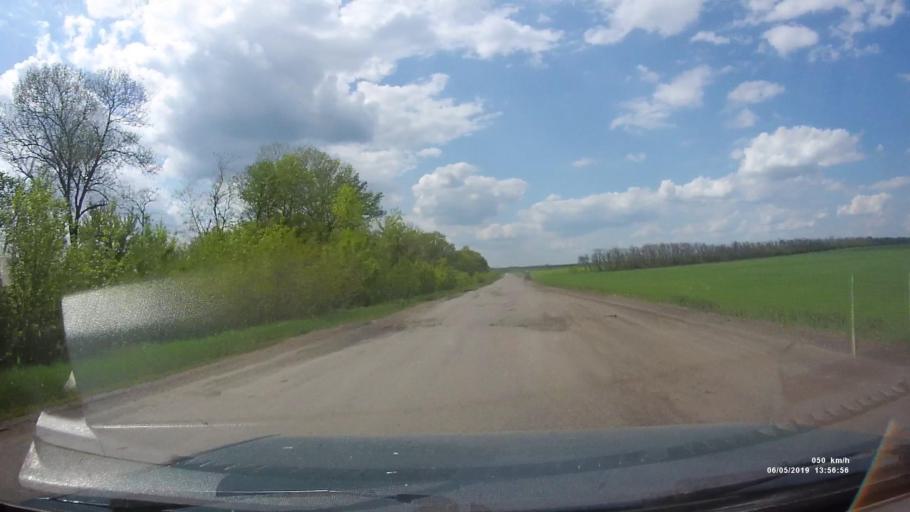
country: RU
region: Rostov
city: Melikhovskaya
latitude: 47.6829
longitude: 40.4266
